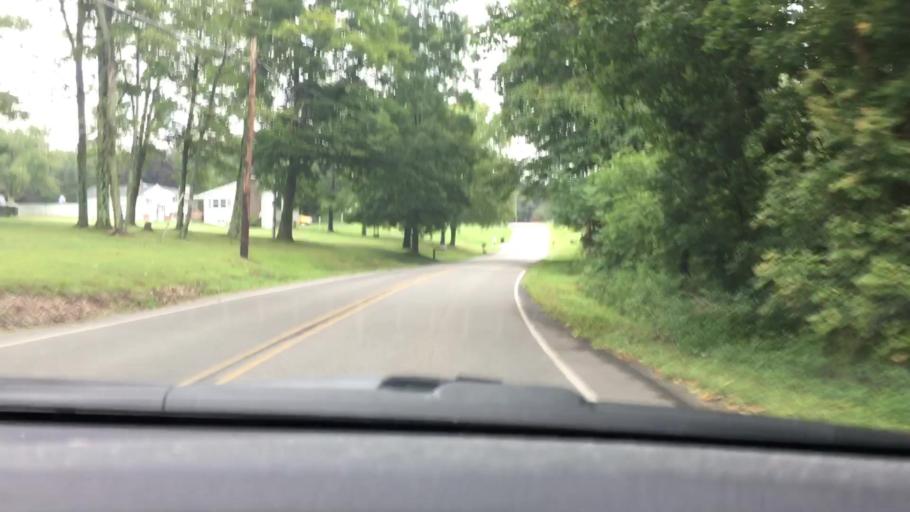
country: US
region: Pennsylvania
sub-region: Butler County
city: Zelienople
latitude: 40.7626
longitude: -80.1153
